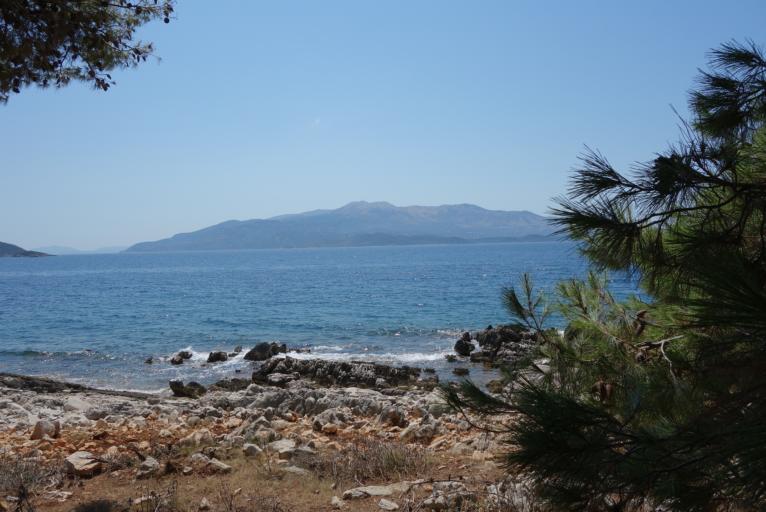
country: AL
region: Vlore
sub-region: Rrethi i Sarandes
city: Xarre
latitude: 39.7877
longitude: 20.0051
